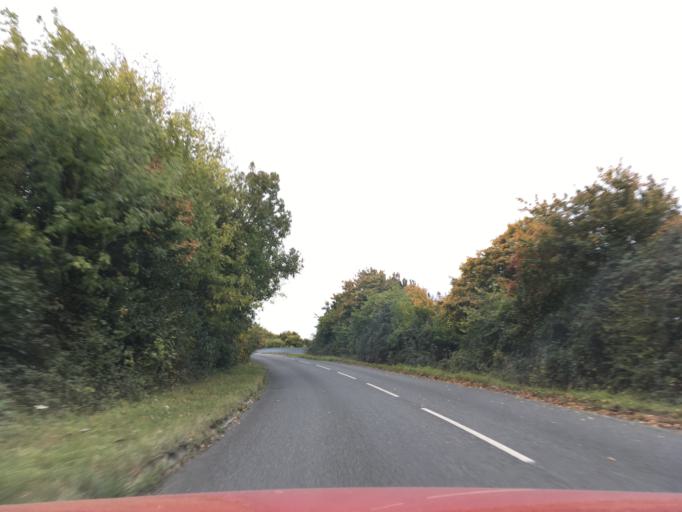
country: GB
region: England
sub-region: Gloucestershire
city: Stonehouse
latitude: 51.7649
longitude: -2.3184
